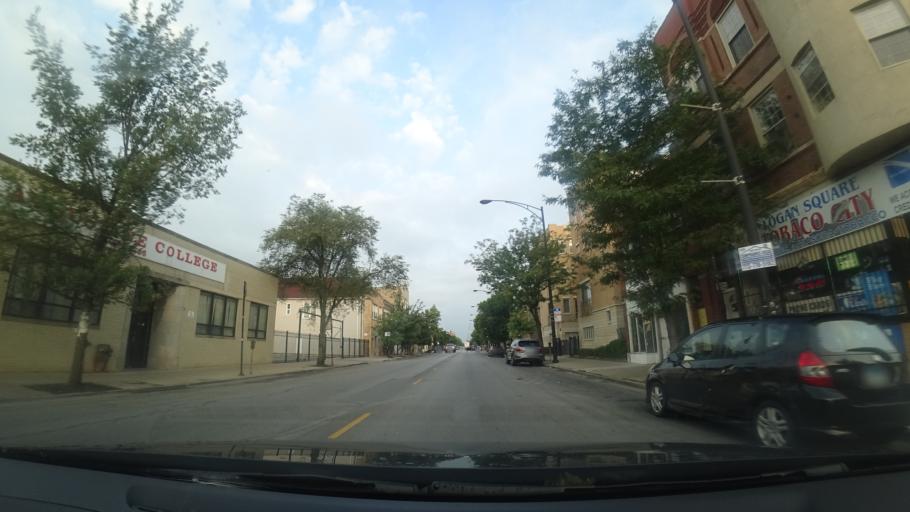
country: US
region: Illinois
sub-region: Cook County
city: Oak Park
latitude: 41.9174
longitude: -87.7090
